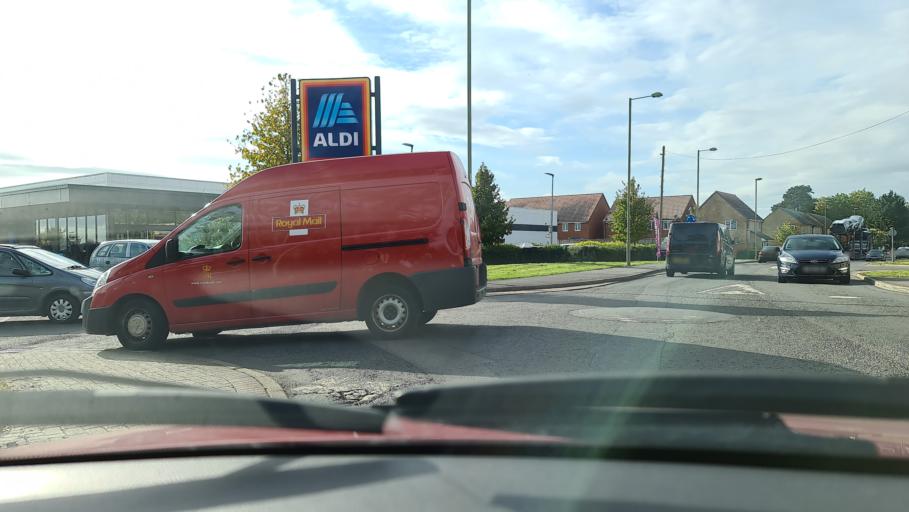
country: GB
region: England
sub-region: Oxfordshire
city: Bicester
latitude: 51.8992
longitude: -1.1413
